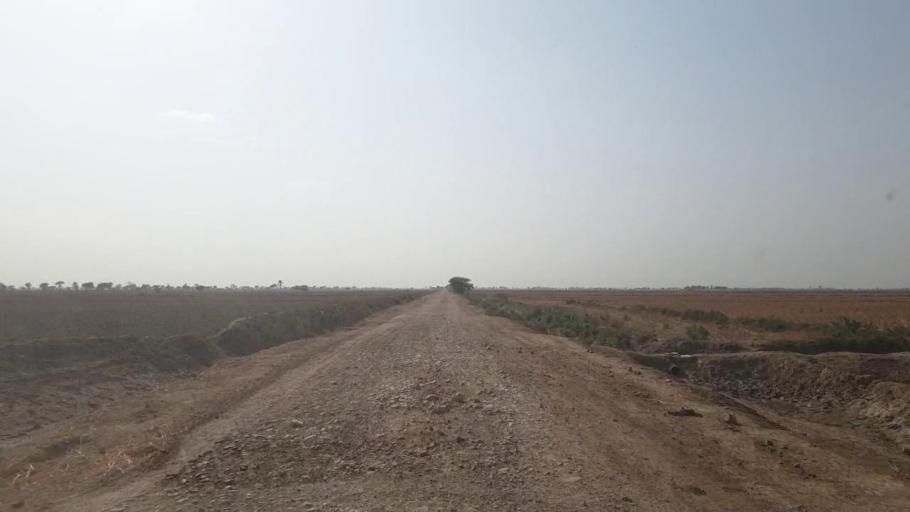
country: PK
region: Sindh
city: Kario
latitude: 24.5589
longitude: 68.5326
